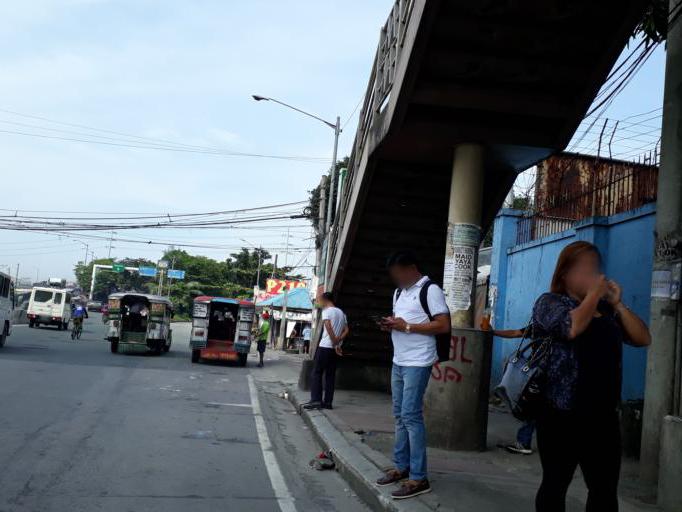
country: PH
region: Calabarzon
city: Del Monte
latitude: 14.6636
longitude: 121.0023
